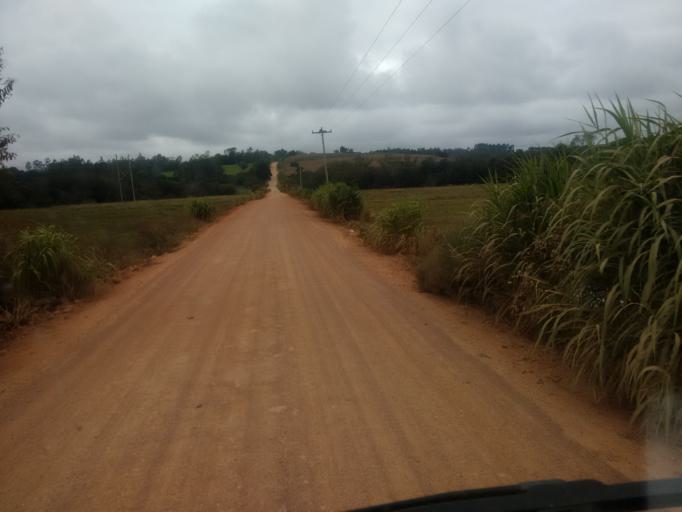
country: BR
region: Rio Grande do Sul
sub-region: Camaqua
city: Camaqua
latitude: -30.7586
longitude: -51.8677
